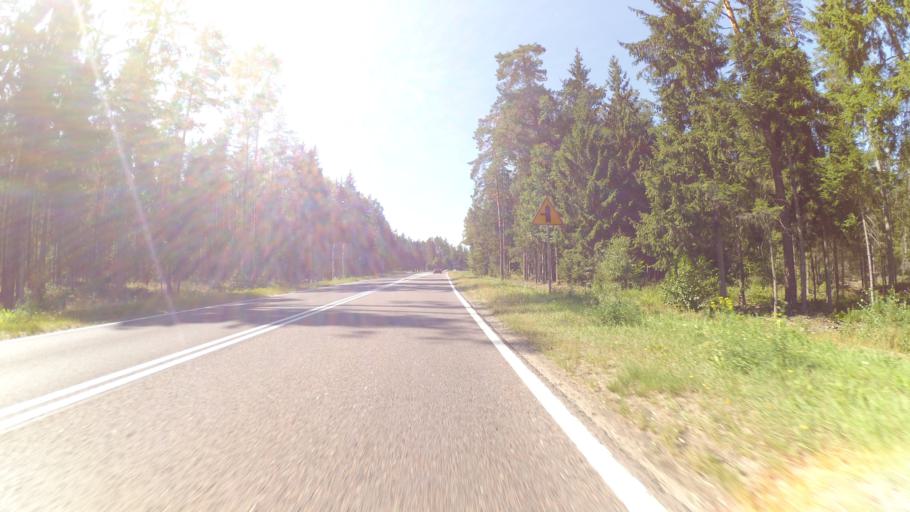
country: PL
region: Podlasie
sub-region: Powiat bialostocki
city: Suprasl
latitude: 53.1272
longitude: 23.4220
